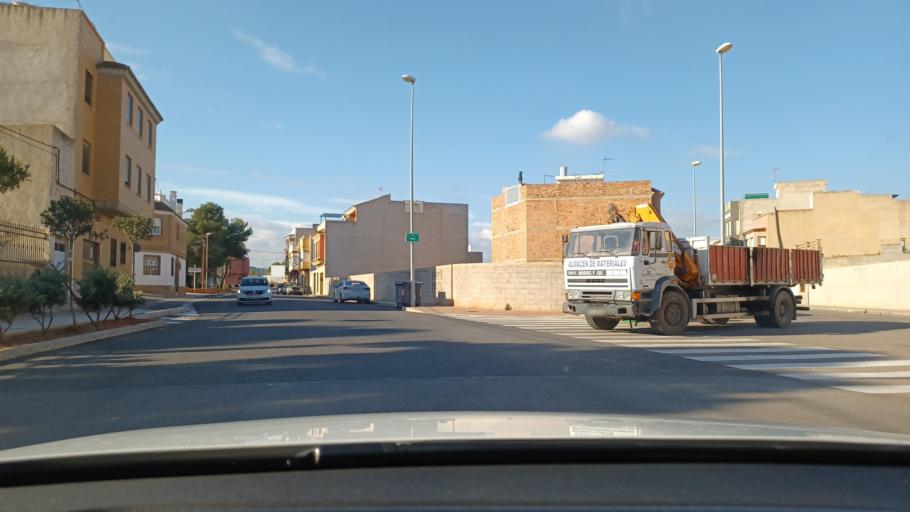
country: ES
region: Valencia
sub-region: Provincia de Castello
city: Betxi
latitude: 39.9310
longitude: -0.1996
